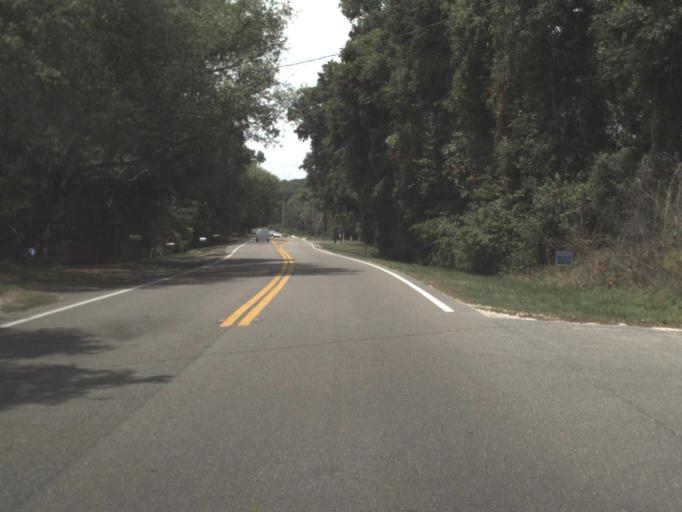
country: US
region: Florida
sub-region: Clay County
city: Keystone Heights
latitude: 29.7731
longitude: -82.0424
